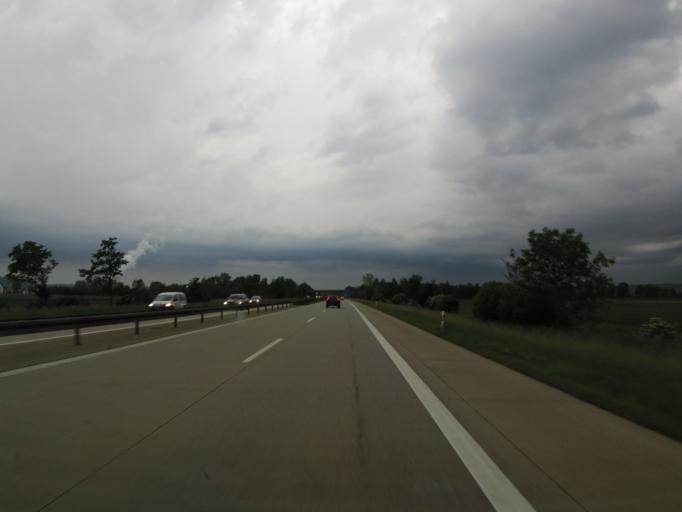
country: DE
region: Bavaria
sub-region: Lower Bavaria
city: Worth an der Isar
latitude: 48.6328
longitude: 12.3409
